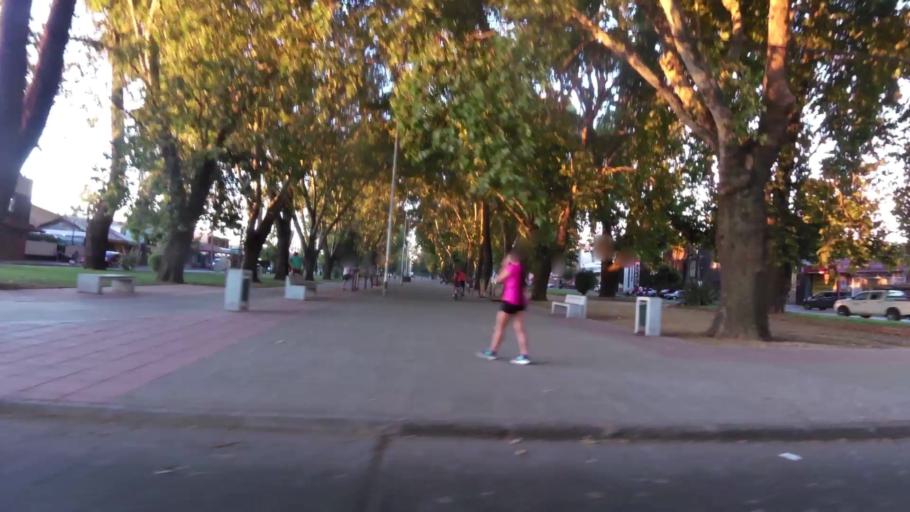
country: CL
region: Maule
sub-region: Provincia de Curico
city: Curico
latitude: -34.9916
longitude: -71.2334
